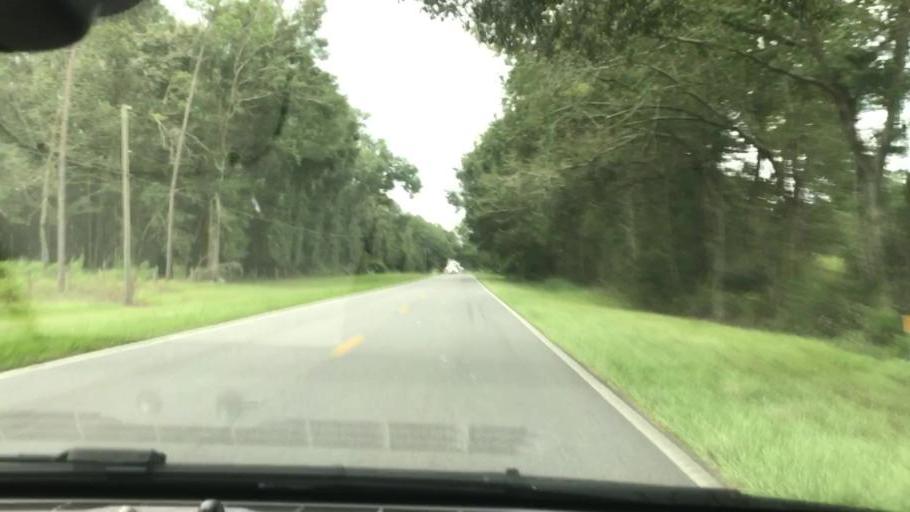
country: US
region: Florida
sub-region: Madison County
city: Madison
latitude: 30.4040
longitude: -83.3004
